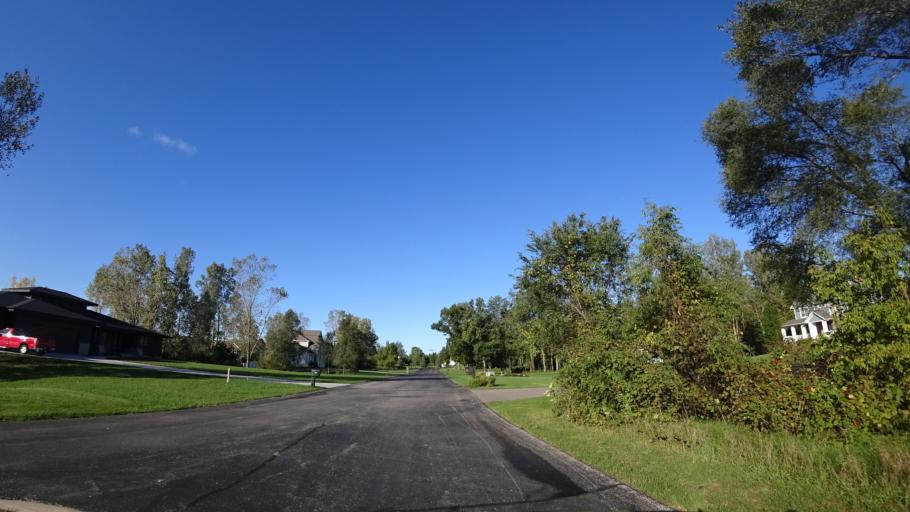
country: US
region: Michigan
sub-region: Kent County
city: Grandville
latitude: 42.9384
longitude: -85.7656
